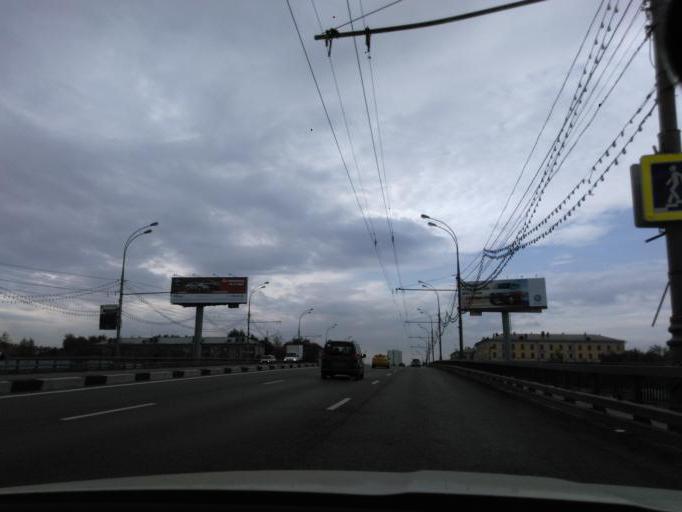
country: RU
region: Moscow
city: Novovladykino
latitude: 55.8489
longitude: 37.5846
